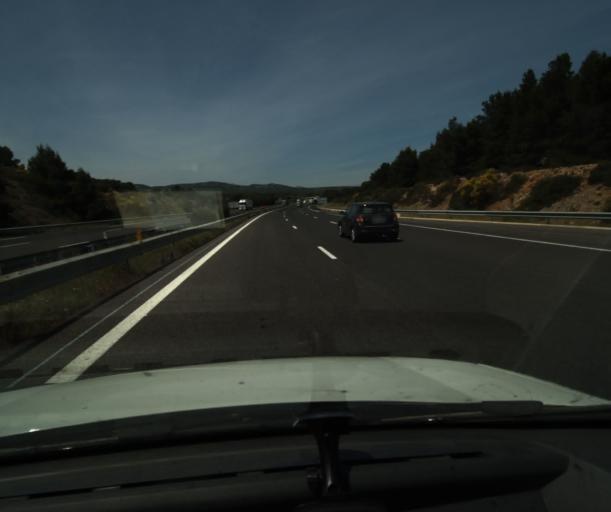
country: FR
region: Languedoc-Roussillon
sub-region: Departement de l'Aude
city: Leucate
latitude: 42.9256
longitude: 2.9724
